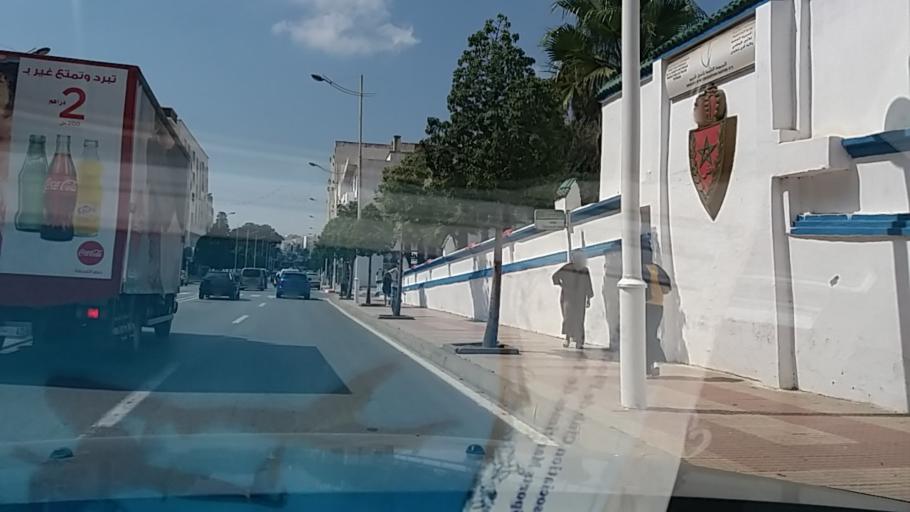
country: MA
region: Tanger-Tetouan
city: Tetouan
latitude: 35.5748
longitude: -5.3450
